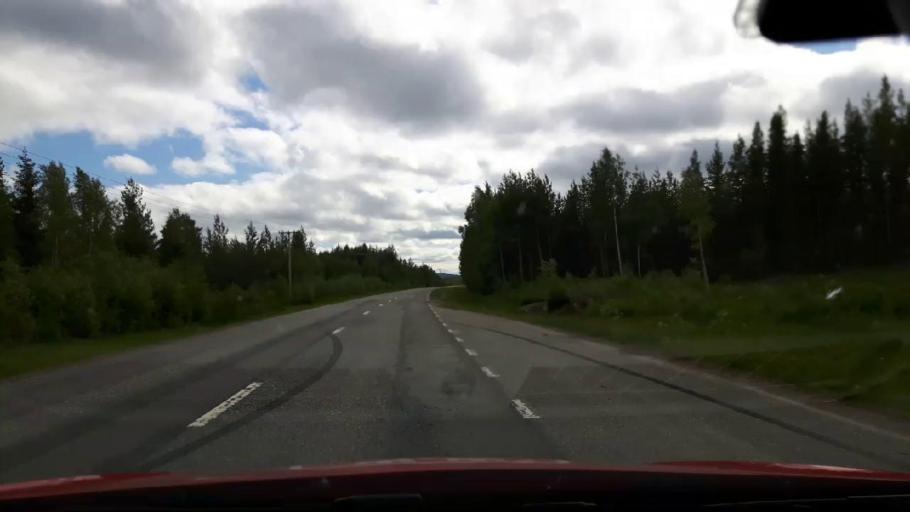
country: SE
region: Jaemtland
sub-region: Ragunda Kommun
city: Hammarstrand
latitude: 63.0018
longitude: 16.1129
